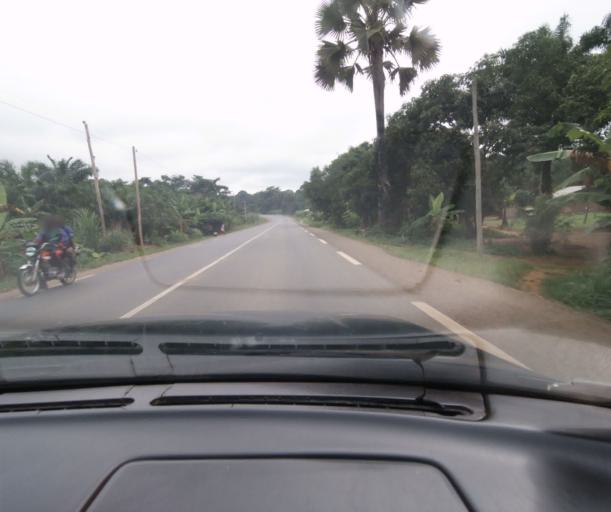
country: CM
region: Centre
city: Saa
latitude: 4.3403
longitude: 11.2835
